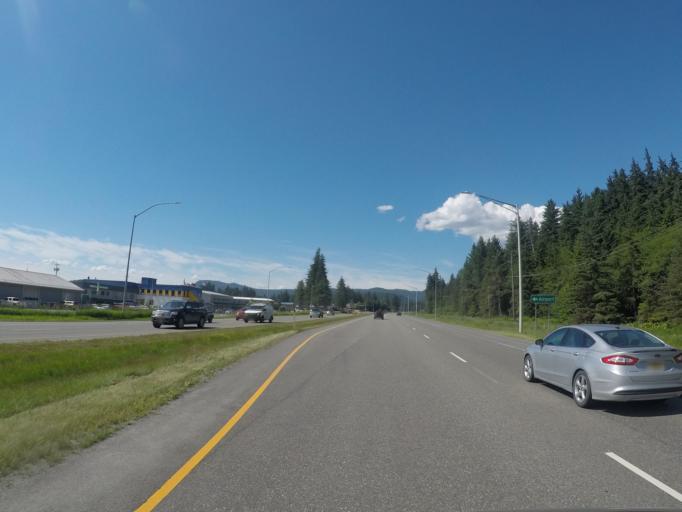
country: US
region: Alaska
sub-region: Juneau City and Borough
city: Juneau
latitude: 58.3617
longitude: -134.5703
